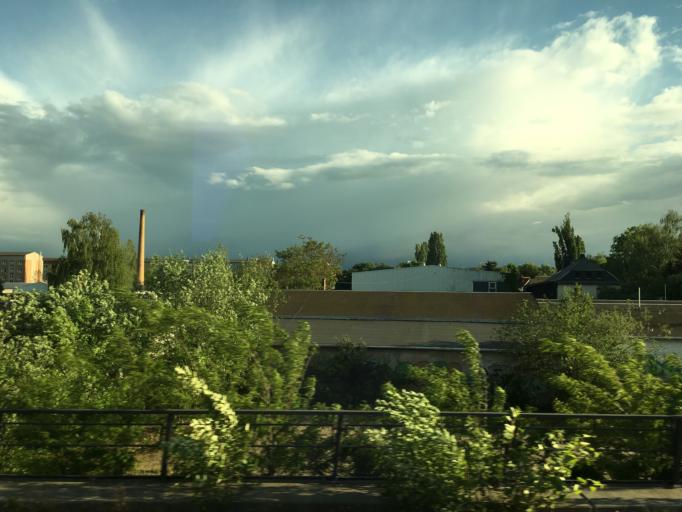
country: DE
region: Saxony
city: Radebeul
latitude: 51.1023
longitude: 13.6625
